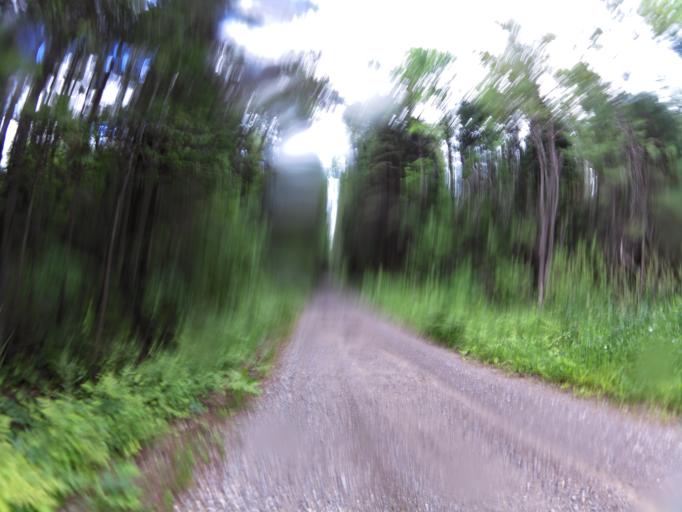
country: CA
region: Ontario
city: Renfrew
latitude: 45.0871
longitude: -76.7207
